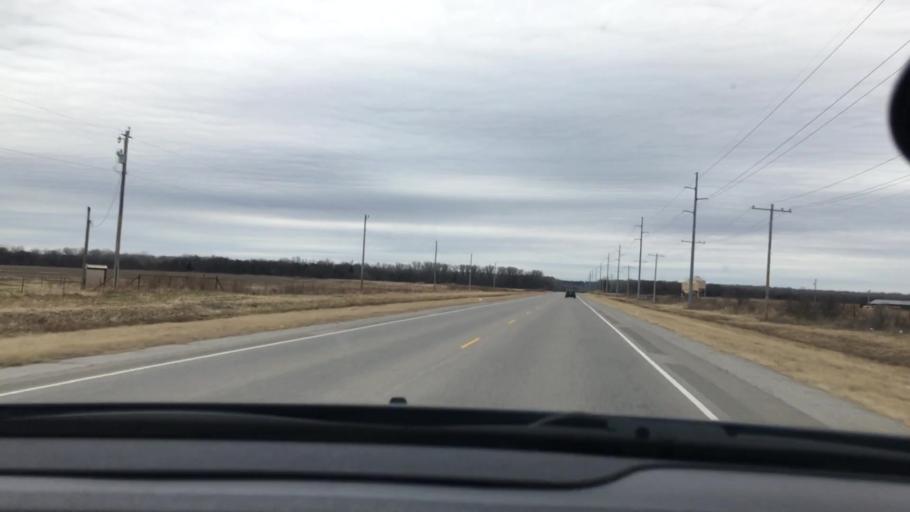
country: US
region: Oklahoma
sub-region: Marshall County
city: Oakland
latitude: 34.2065
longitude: -96.8022
